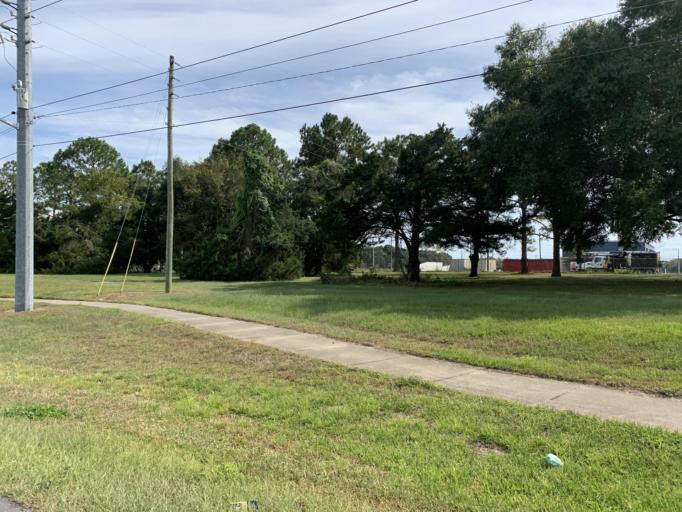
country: US
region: Florida
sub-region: Marion County
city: Ocala
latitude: 29.1643
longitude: -82.0767
